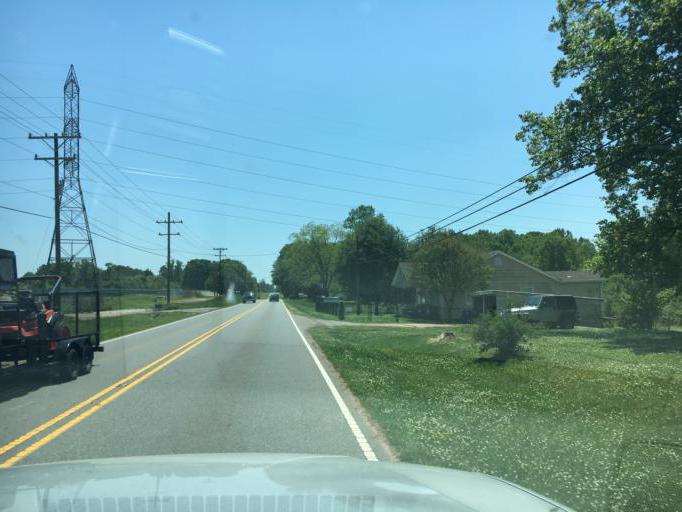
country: US
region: North Carolina
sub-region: Cleveland County
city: Shelby
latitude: 35.2335
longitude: -81.5662
